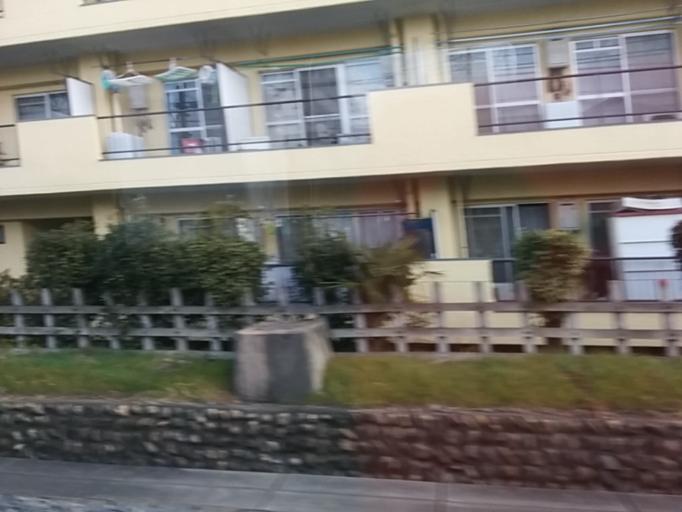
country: JP
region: Saitama
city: Kamifukuoka
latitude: 35.8864
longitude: 139.5011
